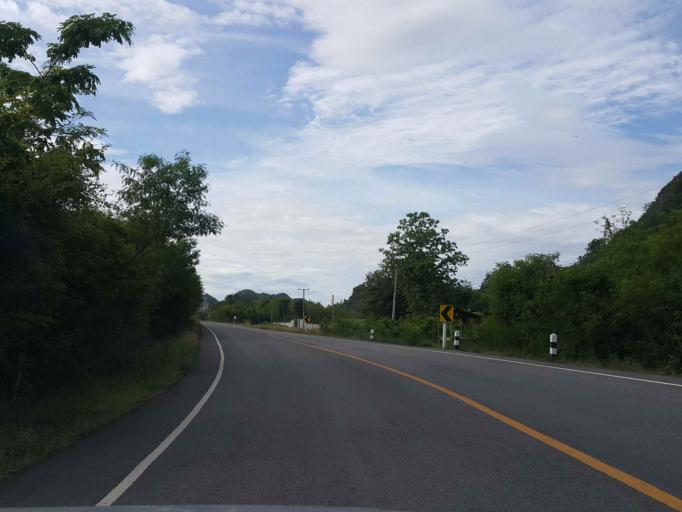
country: TH
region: Sukhothai
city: Thung Saliam
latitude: 17.2817
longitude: 99.5274
